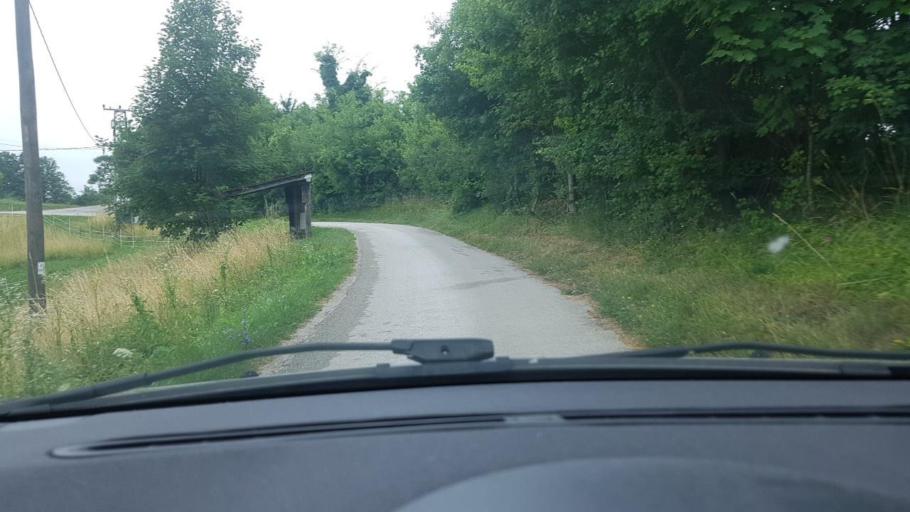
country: SI
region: Videm
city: Videm pri Ptuju
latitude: 46.3355
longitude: 15.9163
